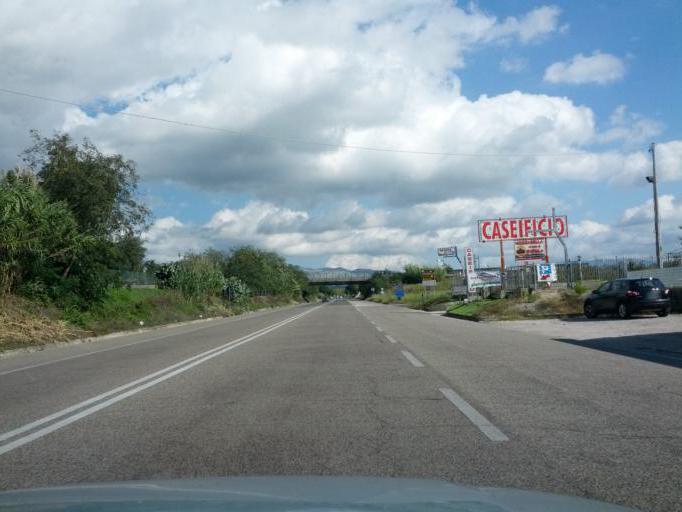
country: IT
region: Latium
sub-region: Provincia di Latina
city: Penitro
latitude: 41.2734
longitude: 13.6949
